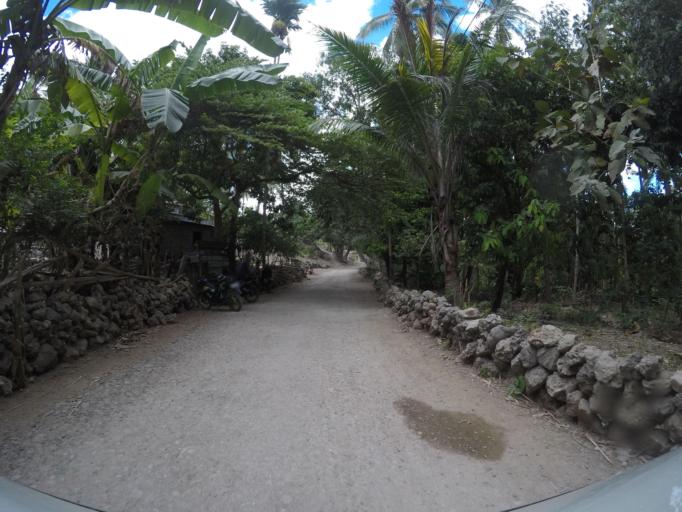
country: TL
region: Lautem
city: Lospalos
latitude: -8.3805
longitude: 126.9227
